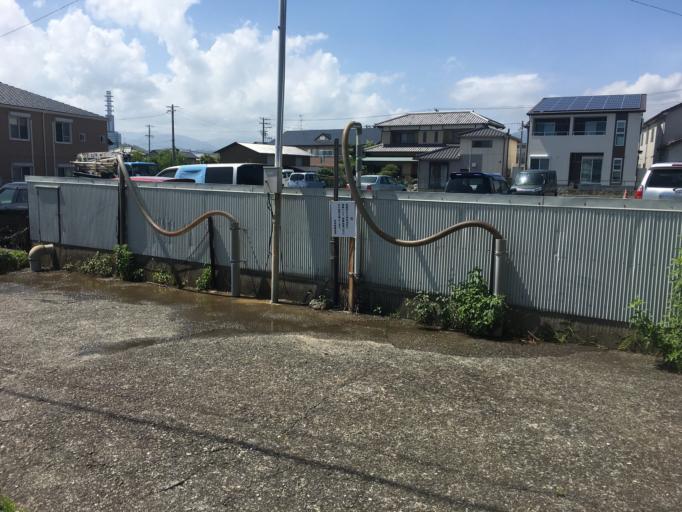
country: JP
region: Shizuoka
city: Shizuoka-shi
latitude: 34.9805
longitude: 138.4280
